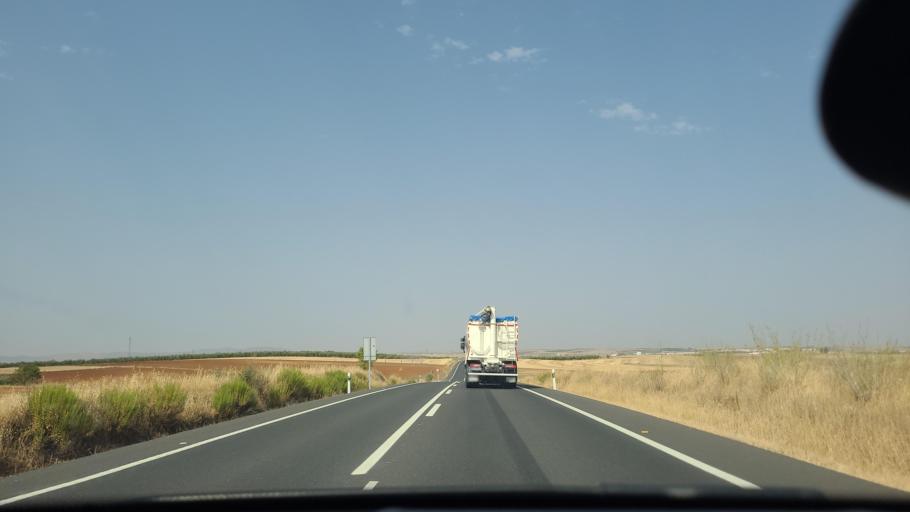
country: ES
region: Extremadura
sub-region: Provincia de Badajoz
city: Berlanga
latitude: 38.2666
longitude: -5.7761
